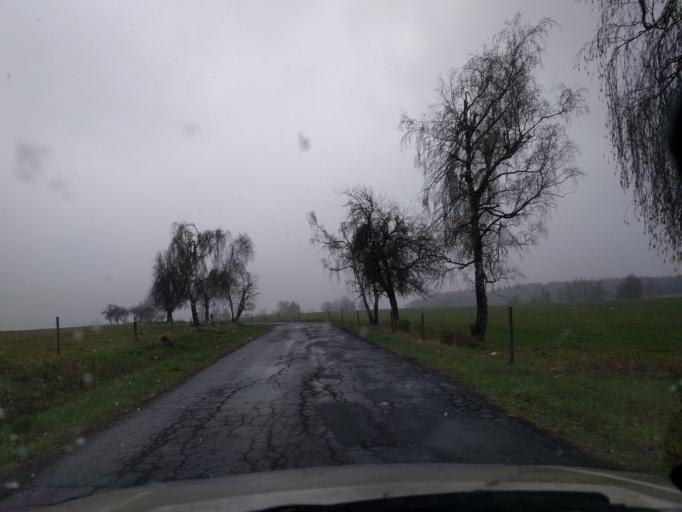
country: CZ
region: Karlovarsky
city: Bochov
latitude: 50.1257
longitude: 13.0840
